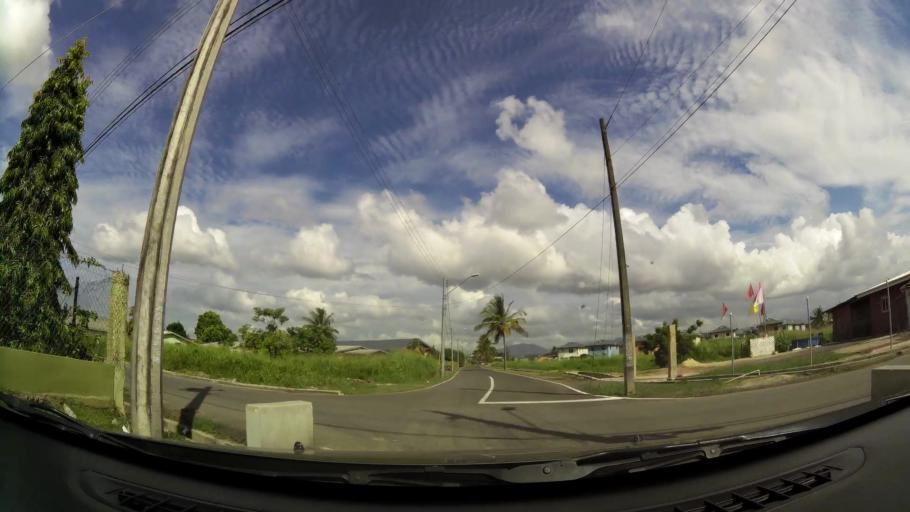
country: TT
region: Chaguanas
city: Chaguanas
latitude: 10.5417
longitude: -61.3896
